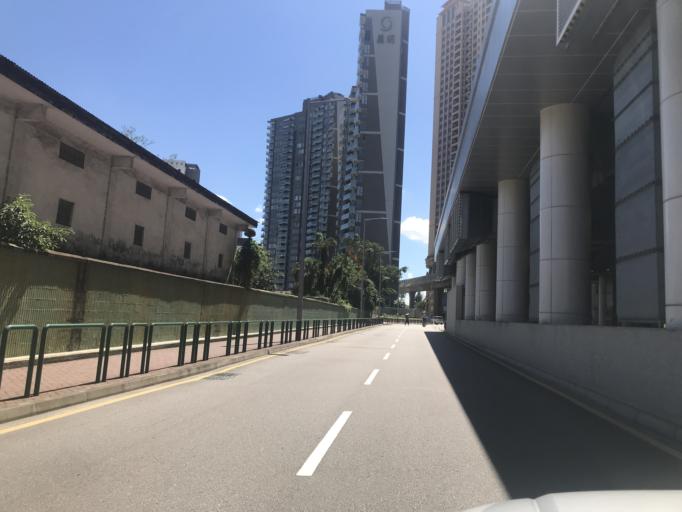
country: MO
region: Macau
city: Macau
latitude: 22.1569
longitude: 113.5462
